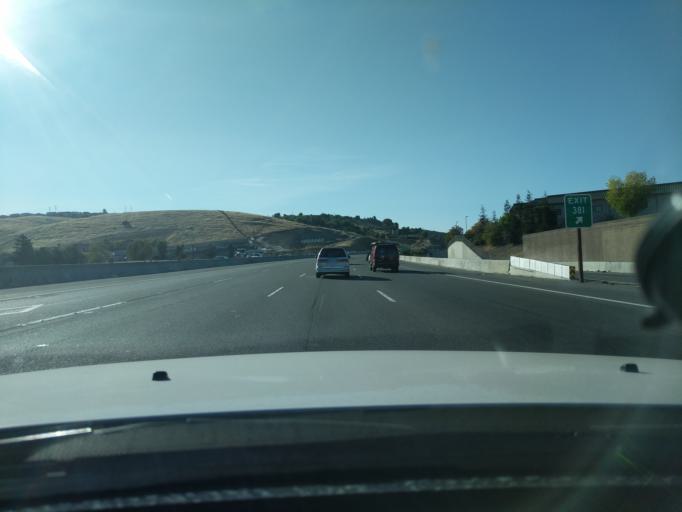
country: US
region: California
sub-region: Santa Clara County
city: Seven Trees
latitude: 37.2973
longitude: -121.8114
